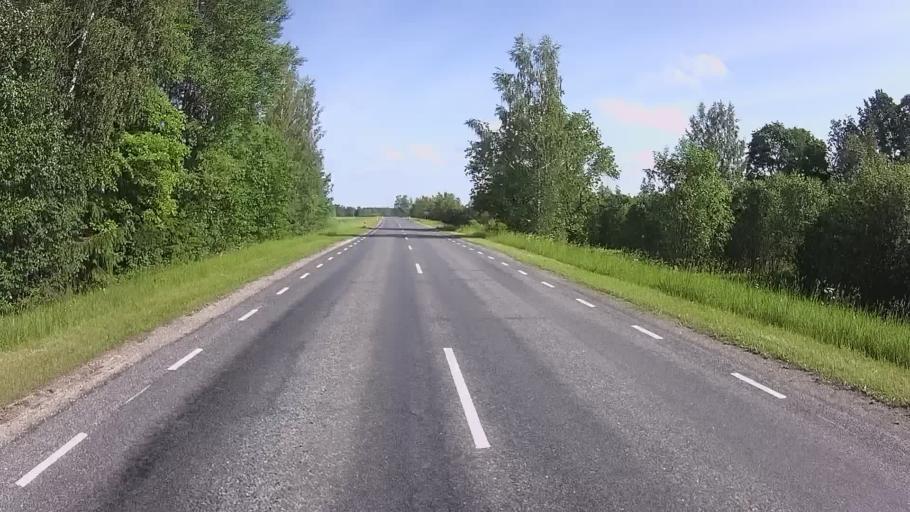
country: EE
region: Valgamaa
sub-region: Torva linn
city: Torva
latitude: 58.0796
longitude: 26.0418
